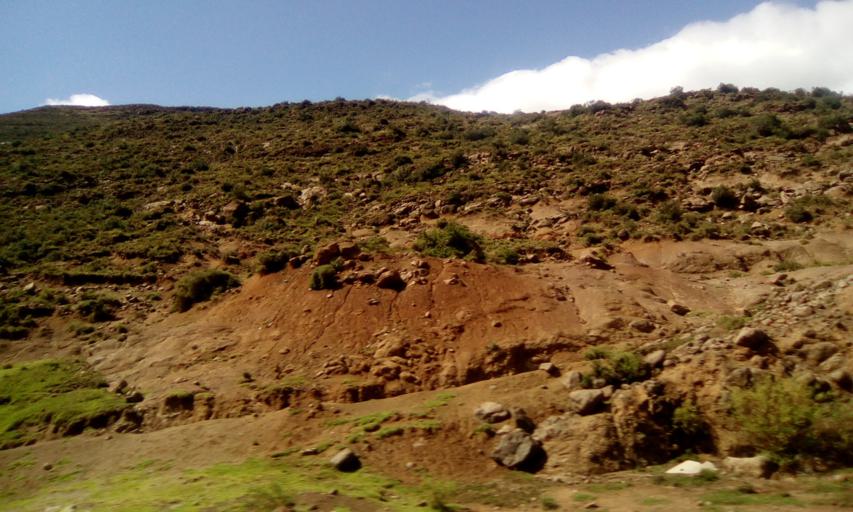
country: LS
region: Maseru
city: Nako
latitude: -29.6560
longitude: 27.8406
